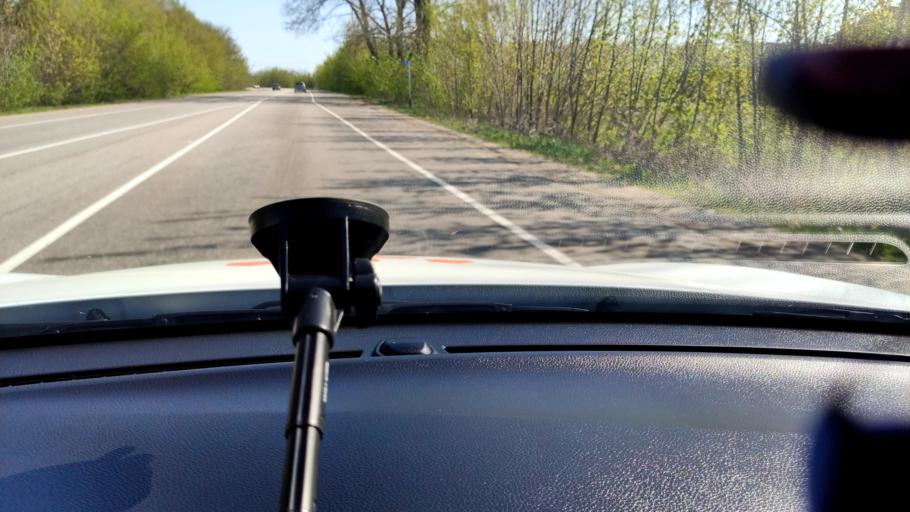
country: RU
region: Voronezj
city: Devitsa
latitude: 51.6005
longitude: 38.9722
